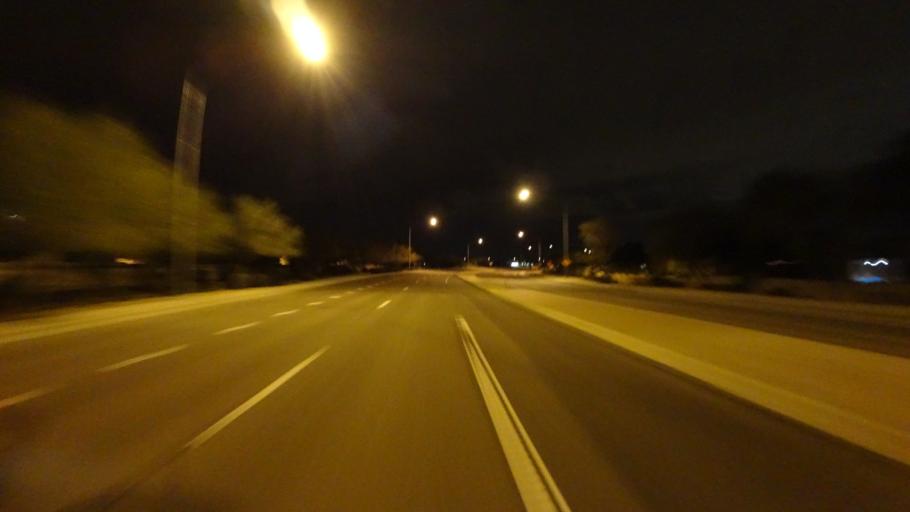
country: US
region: Arizona
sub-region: Pinal County
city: Apache Junction
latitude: 33.3851
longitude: -111.6154
